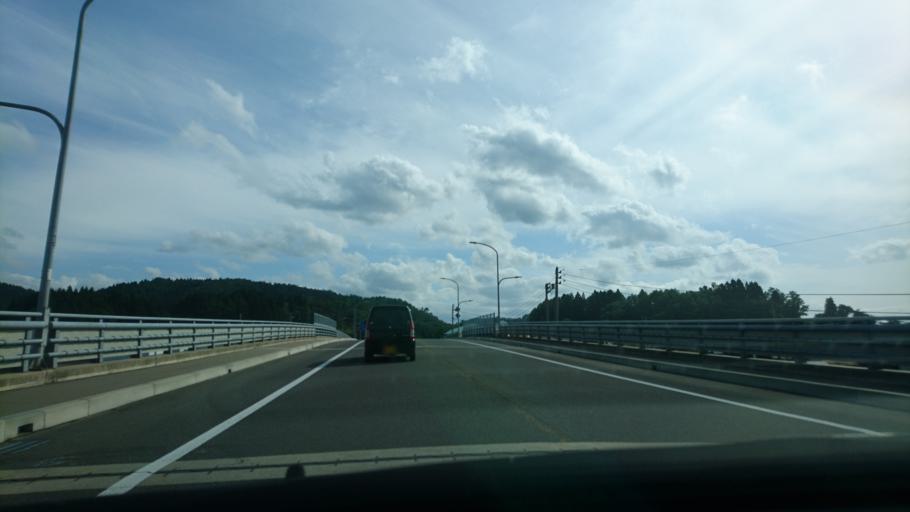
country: JP
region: Akita
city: Yokotemachi
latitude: 39.3074
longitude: 140.5753
